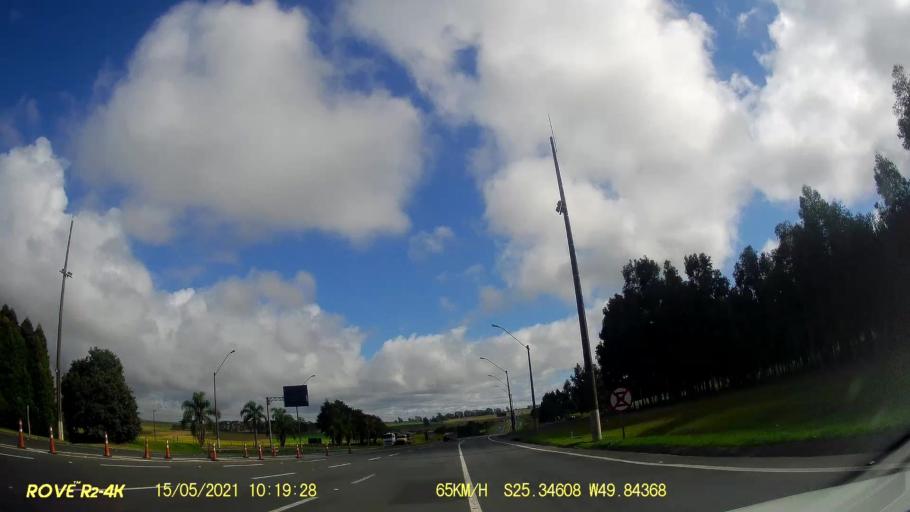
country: BR
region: Parana
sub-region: Palmeira
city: Palmeira
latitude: -25.3457
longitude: -49.8438
